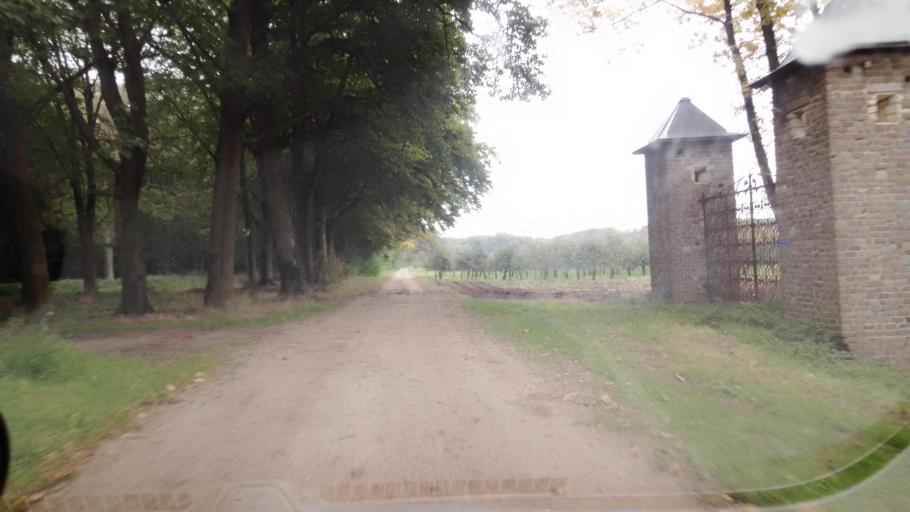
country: NL
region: Limburg
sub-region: Gemeente Venlo
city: Tegelen
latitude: 51.3454
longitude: 6.1088
